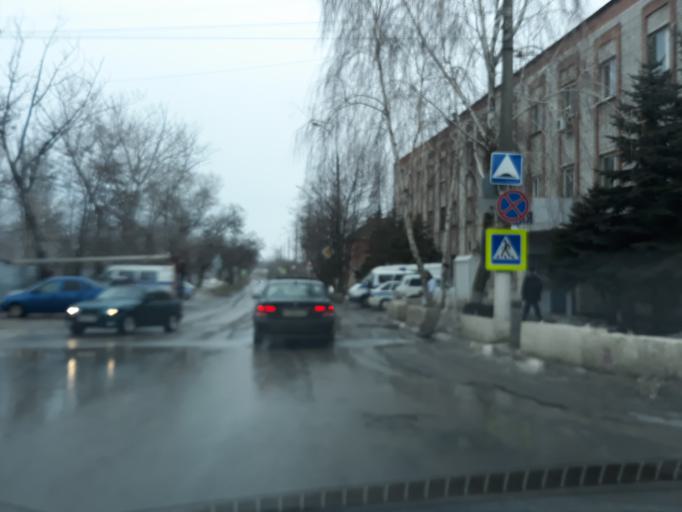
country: RU
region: Rostov
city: Taganrog
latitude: 47.2366
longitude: 38.9210
